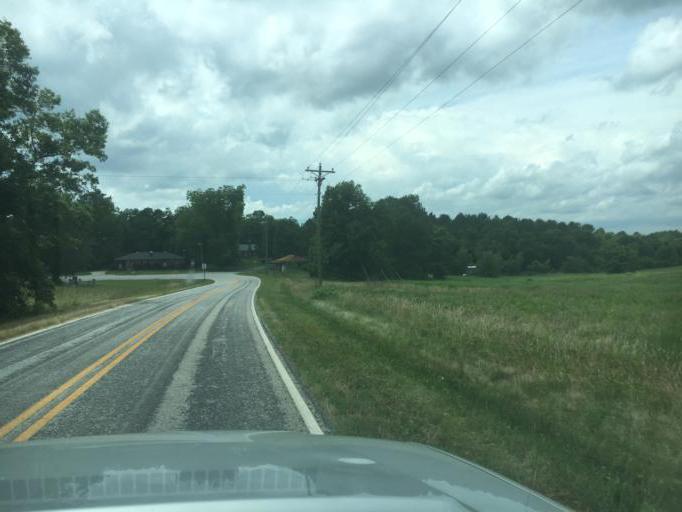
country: US
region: Georgia
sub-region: Hart County
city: Reed Creek
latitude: 34.4601
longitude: -82.9513
